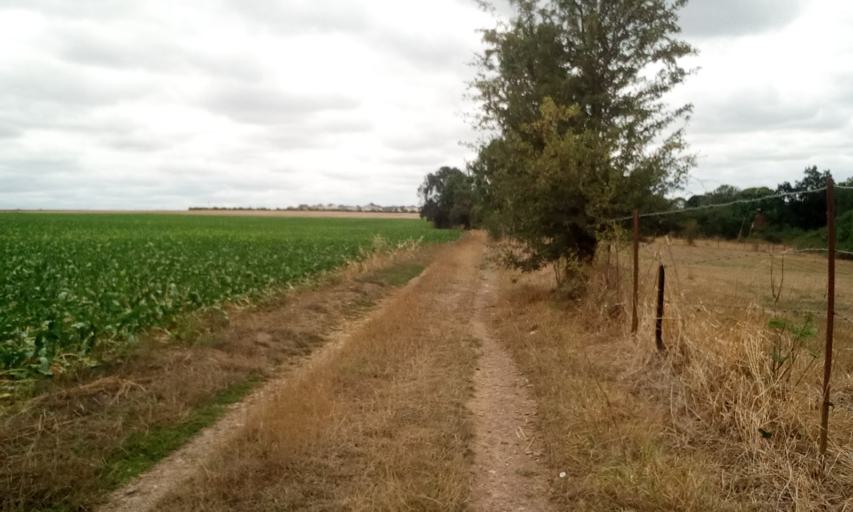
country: FR
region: Lower Normandy
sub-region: Departement du Calvados
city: Eterville
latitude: 49.1534
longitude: -0.4386
